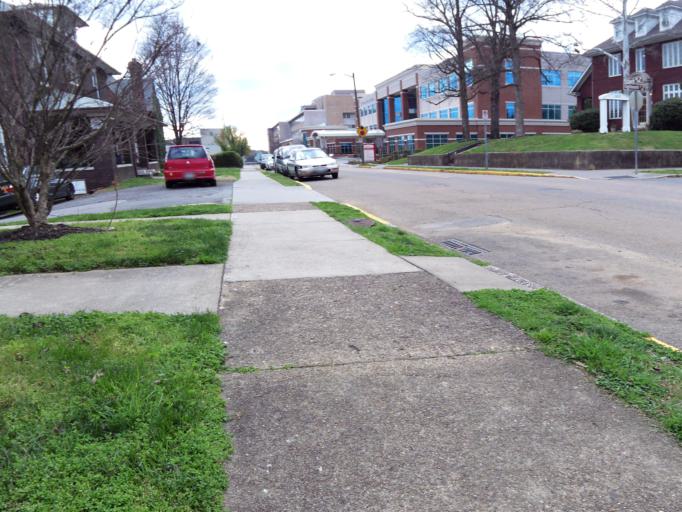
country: US
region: Tennessee
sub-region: Knox County
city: Knoxville
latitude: 35.9577
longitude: -83.9347
